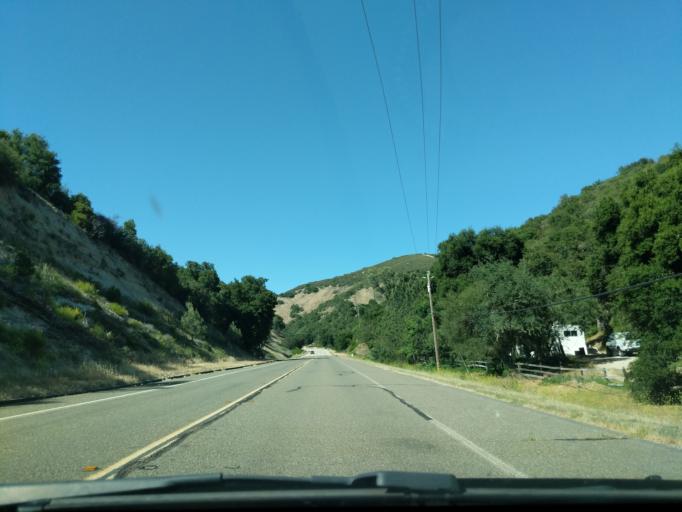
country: US
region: California
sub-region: Monterey County
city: King City
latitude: 36.0704
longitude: -121.1828
